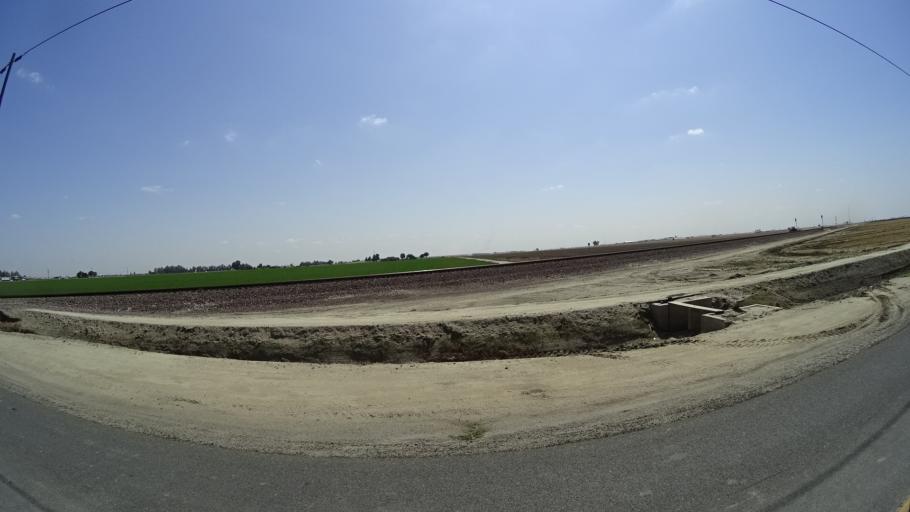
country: US
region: California
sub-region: Kings County
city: Home Garden
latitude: 36.2073
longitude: -119.6370
